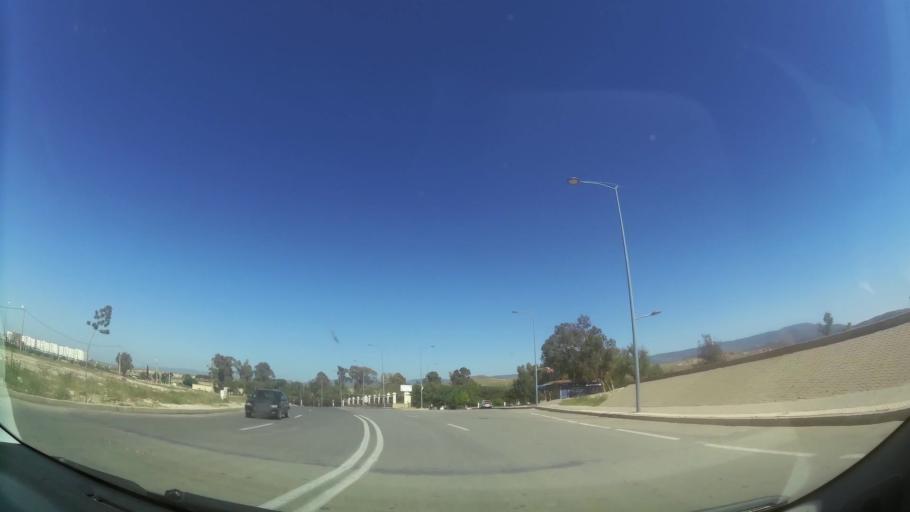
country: MA
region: Oriental
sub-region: Oujda-Angad
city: Oujda
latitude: 34.6665
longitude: -1.8663
